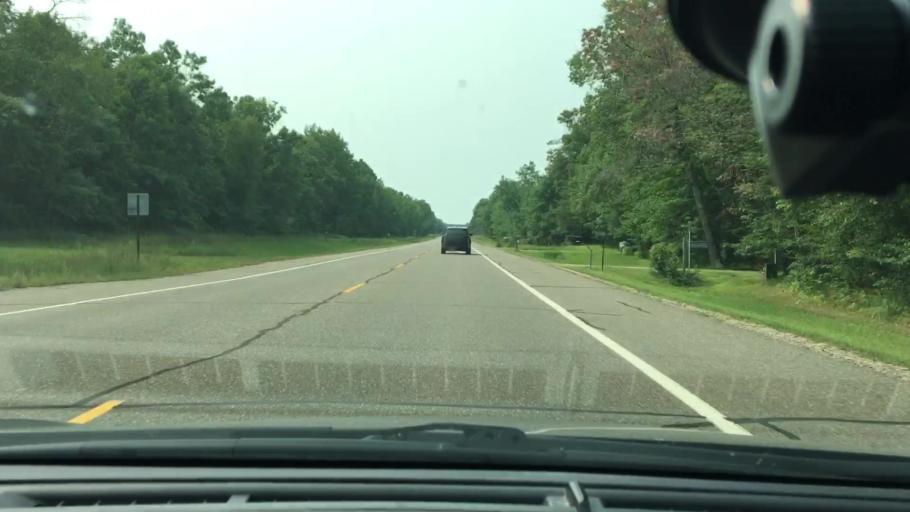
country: US
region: Minnesota
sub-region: Crow Wing County
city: Breezy Point
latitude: 46.5090
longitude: -94.1362
